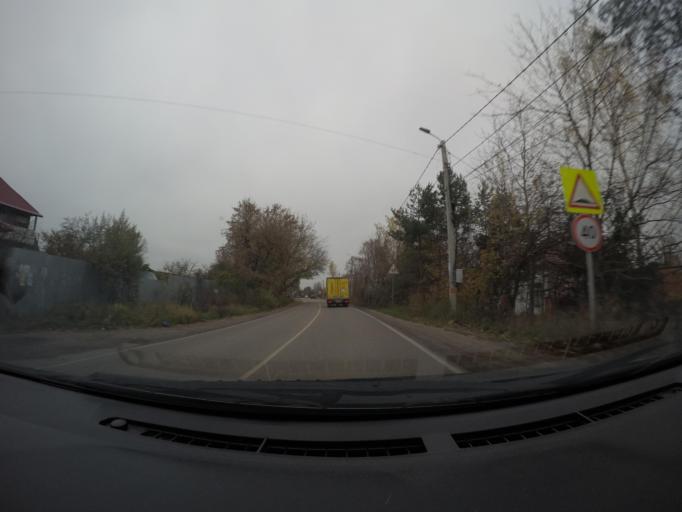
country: RU
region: Moskovskaya
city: Gzhel'
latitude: 55.5804
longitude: 38.3984
